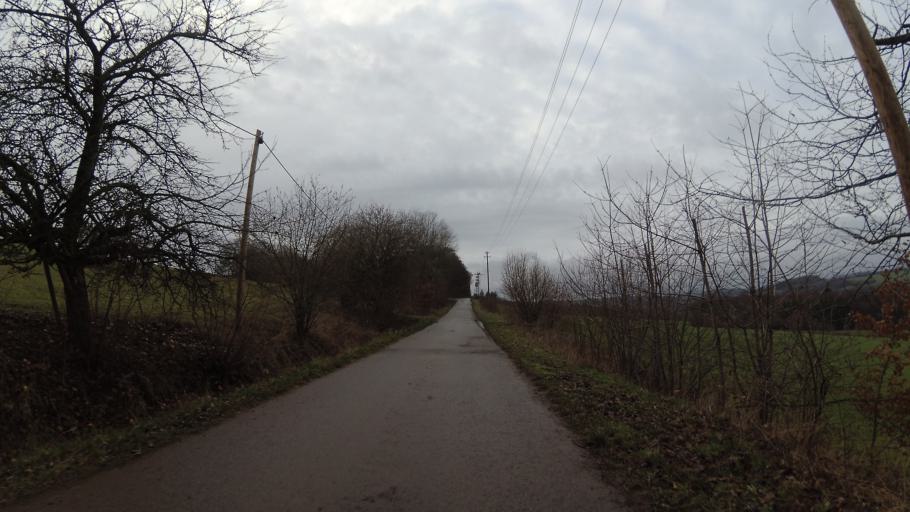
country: DE
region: Rheinland-Pfalz
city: Breitenbach
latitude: 49.4438
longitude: 7.2675
